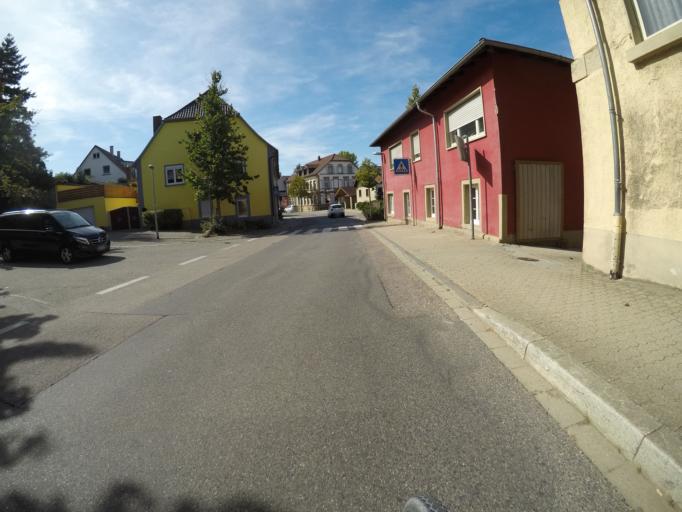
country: DE
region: Baden-Wuerttemberg
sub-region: Karlsruhe Region
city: Oberderdingen
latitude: 49.0868
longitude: 8.7805
